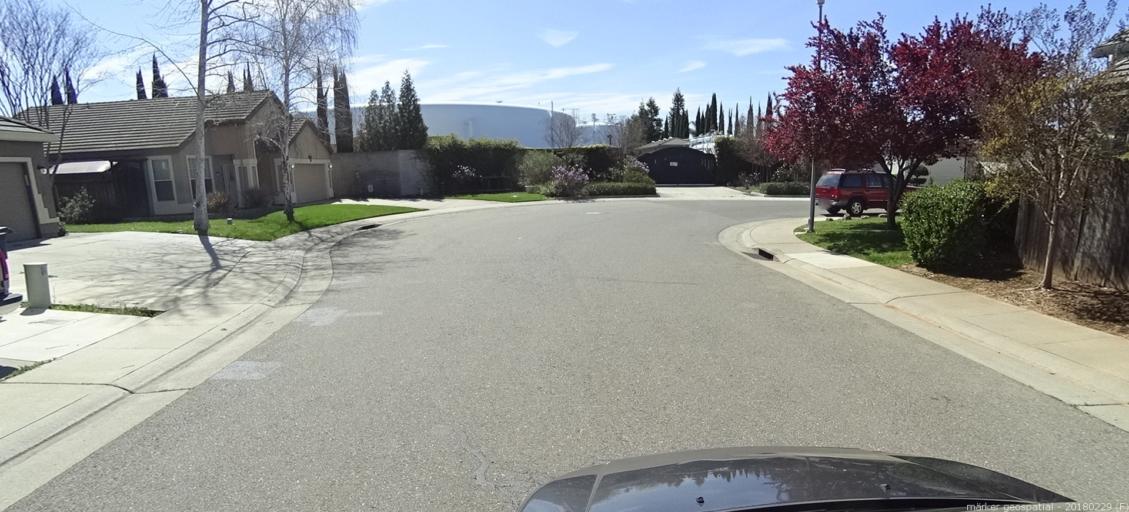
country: US
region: California
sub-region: Sacramento County
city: Rosemont
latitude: 38.5373
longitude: -121.3585
